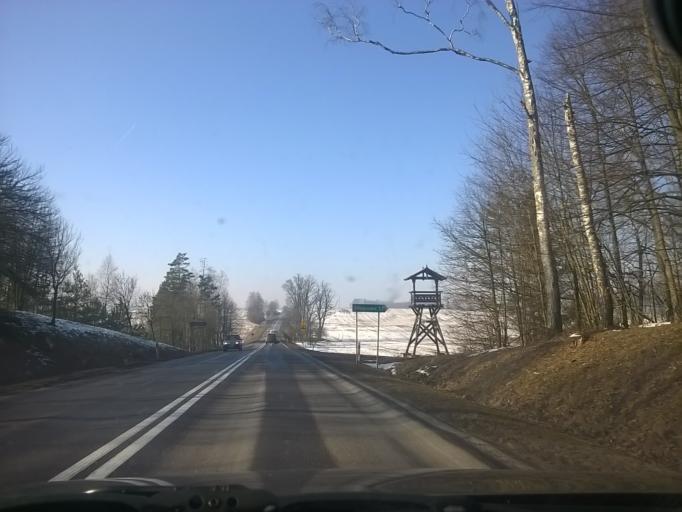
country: PL
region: Warmian-Masurian Voivodeship
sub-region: Powiat mragowski
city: Mragowo
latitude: 53.8399
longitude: 21.1803
